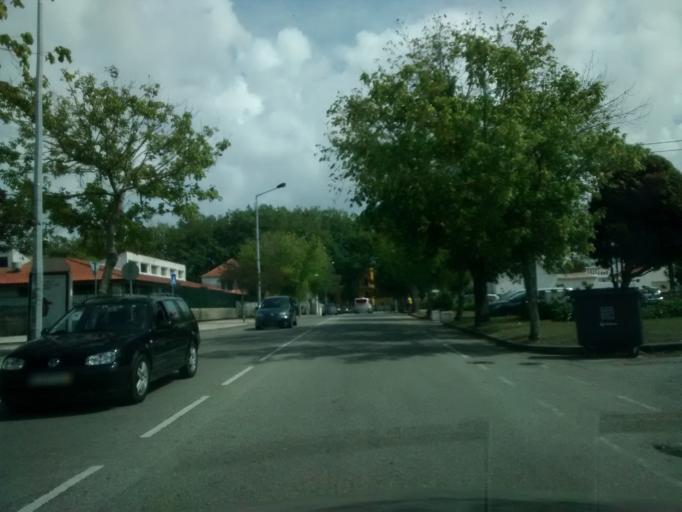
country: PT
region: Aveiro
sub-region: Aveiro
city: Aveiro
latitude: 40.6364
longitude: -8.6565
